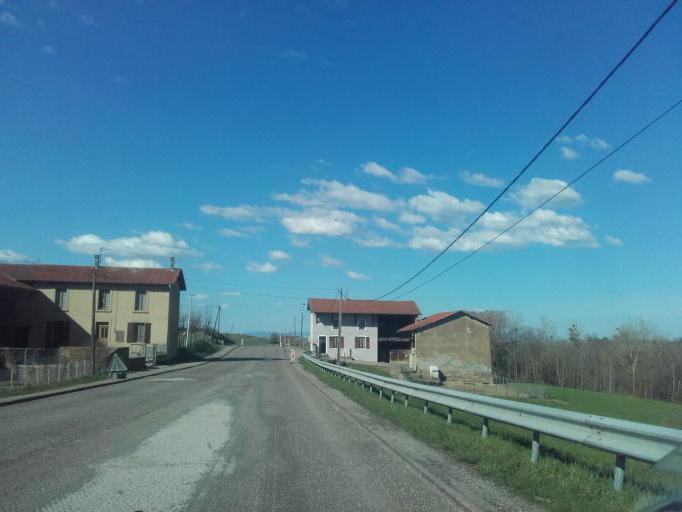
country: FR
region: Rhone-Alpes
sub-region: Departement de l'Isere
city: Champier
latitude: 45.4858
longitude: 5.2936
